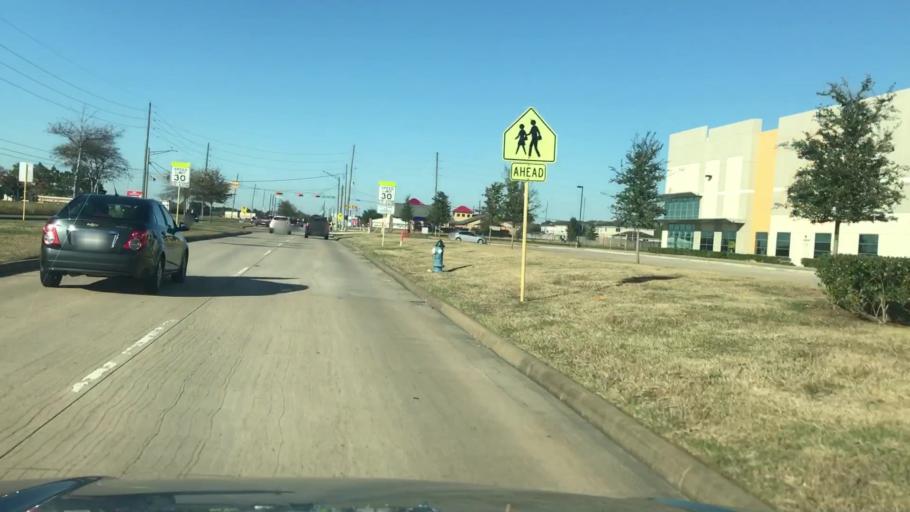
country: US
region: Texas
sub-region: Fort Bend County
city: Cinco Ranch
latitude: 29.8082
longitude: -95.7520
